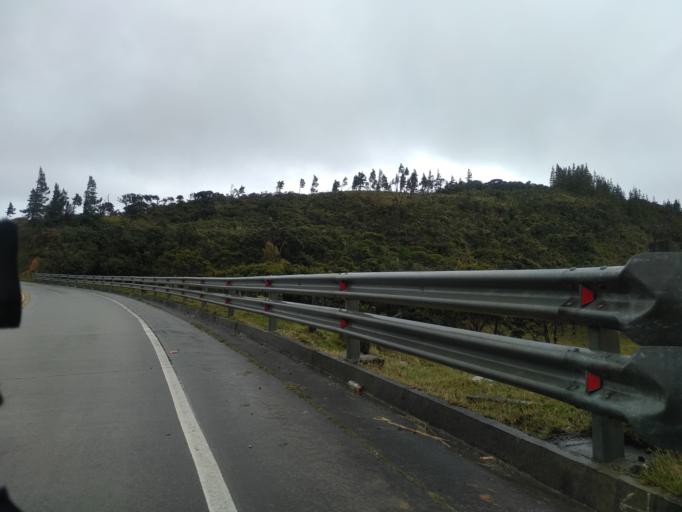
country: EC
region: Loja
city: Loja
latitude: -3.8922
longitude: -79.2622
